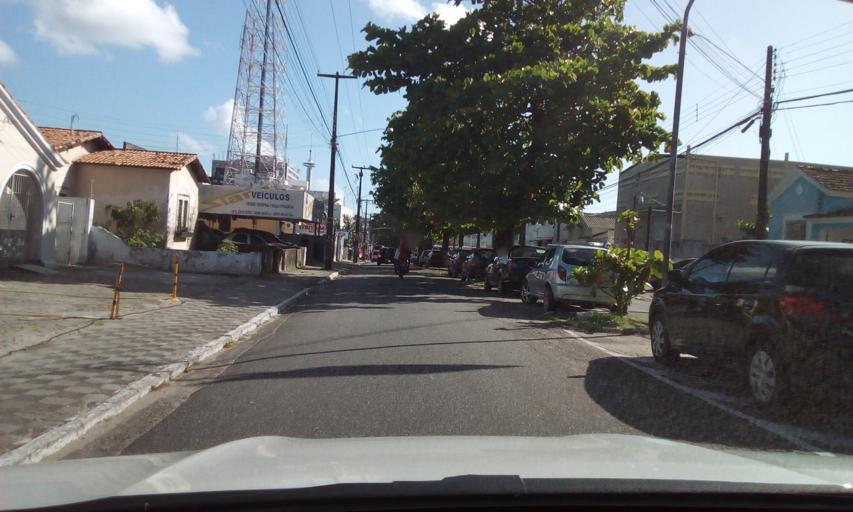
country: BR
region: Paraiba
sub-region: Joao Pessoa
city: Joao Pessoa
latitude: -7.1242
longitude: -34.8783
